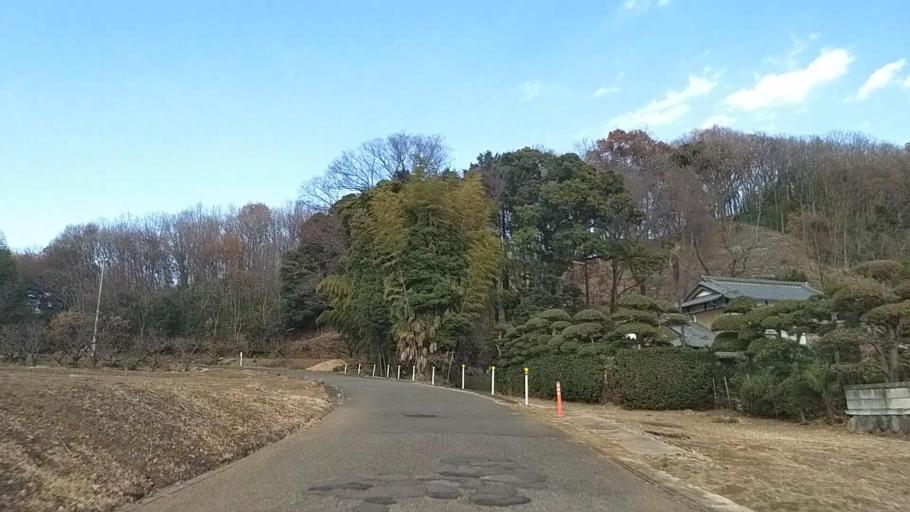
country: JP
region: Kanagawa
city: Isehara
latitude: 35.4180
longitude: 139.3177
